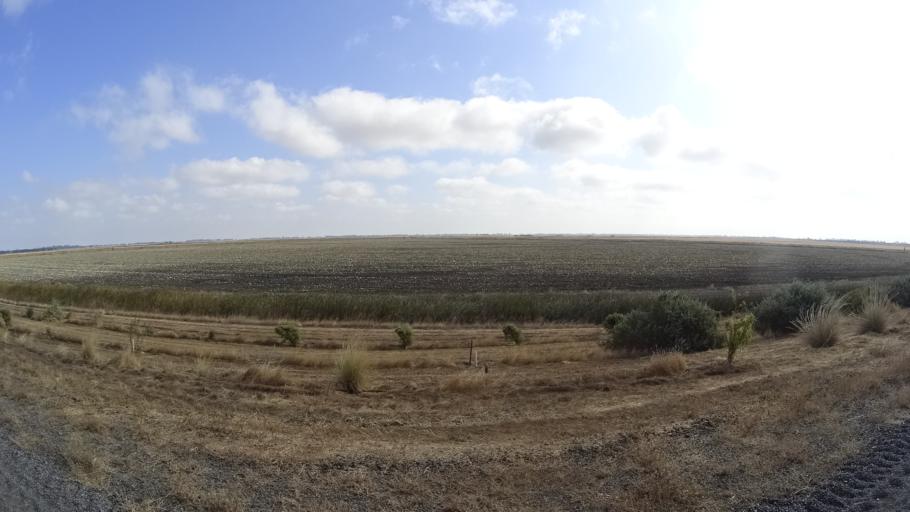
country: US
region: California
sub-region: Yolo County
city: Woodland
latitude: 38.8294
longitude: -121.7960
